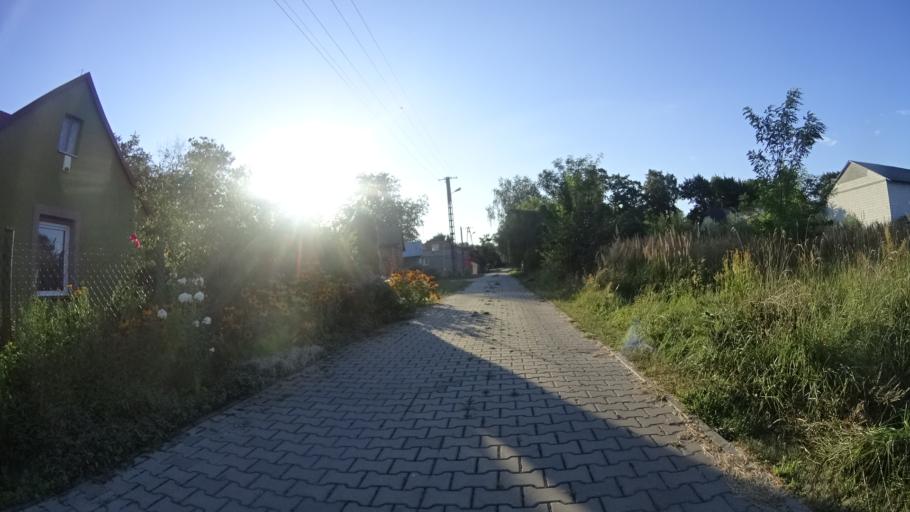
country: PL
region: Masovian Voivodeship
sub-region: Powiat bialobrzeski
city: Wysmierzyce
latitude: 51.6563
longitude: 20.7808
